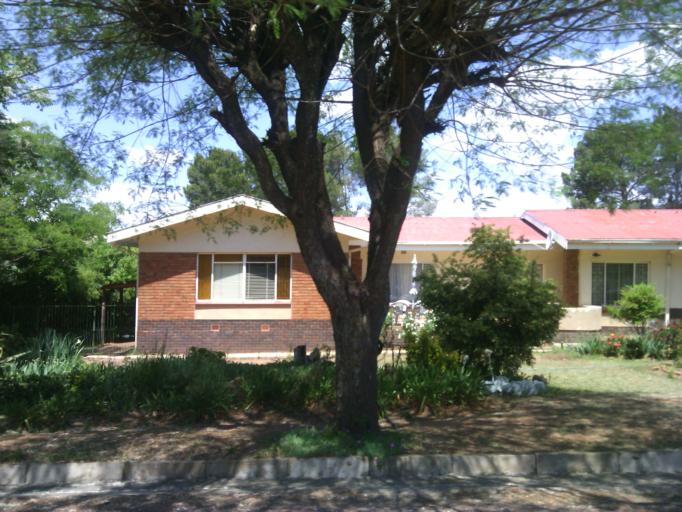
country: ZA
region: Orange Free State
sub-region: Xhariep District Municipality
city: Dewetsdorp
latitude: -29.5792
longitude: 26.6646
